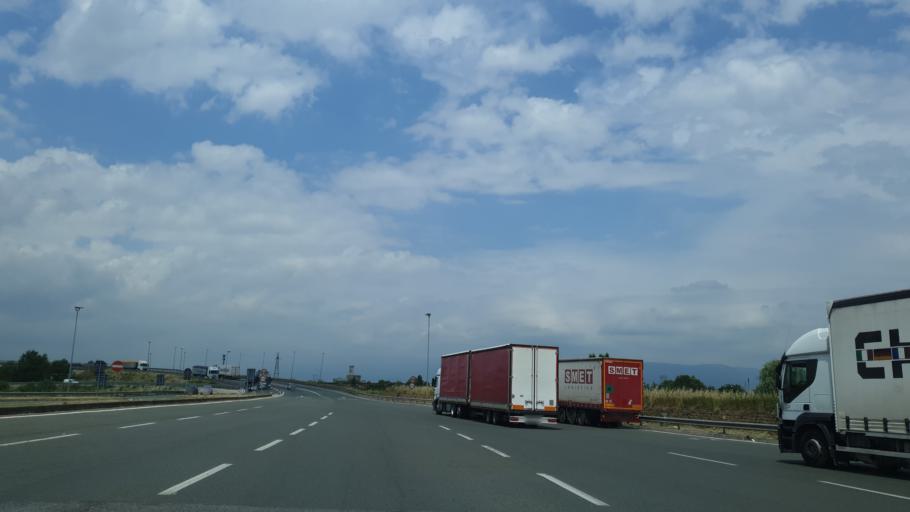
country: IT
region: Tuscany
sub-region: Province of Florence
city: Mantignano-Ugnano
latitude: 43.7762
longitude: 11.1644
